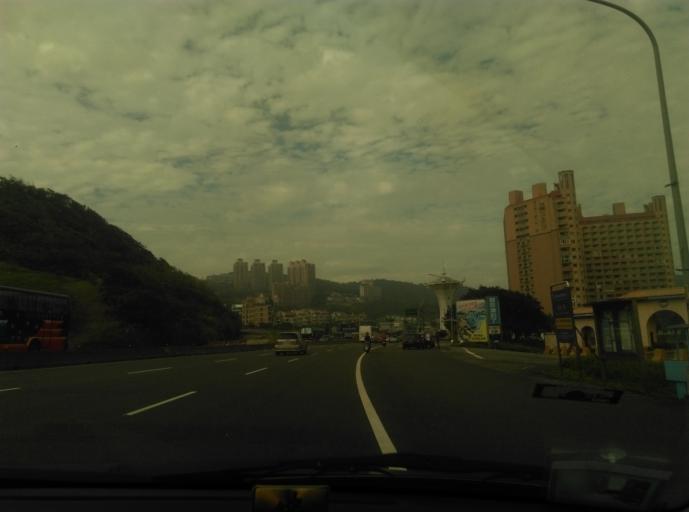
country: TW
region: Taiwan
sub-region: Keelung
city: Keelung
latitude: 25.1859
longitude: 121.6837
